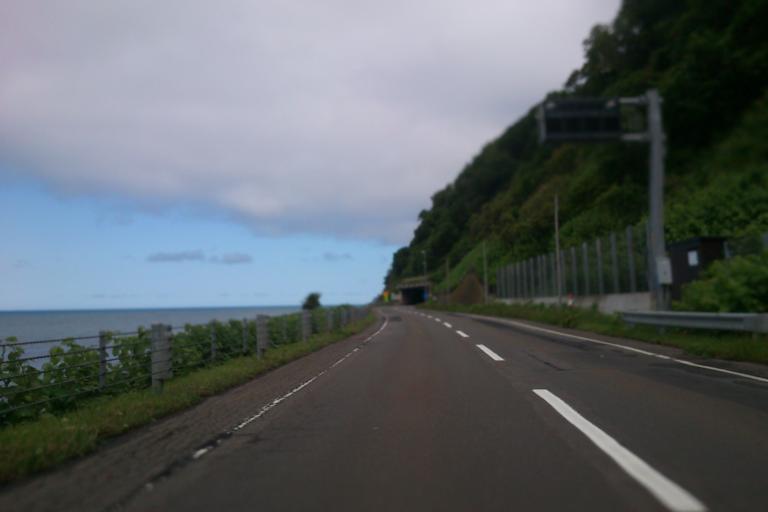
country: JP
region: Hokkaido
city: Ishikari
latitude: 43.4362
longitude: 141.4176
